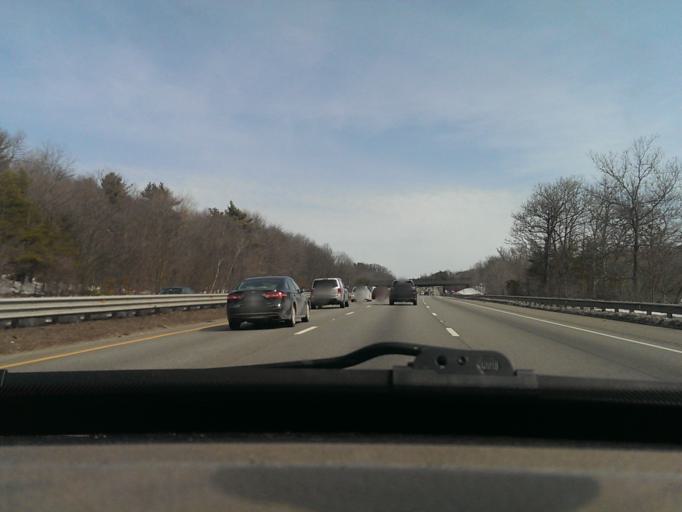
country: US
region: Massachusetts
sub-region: Worcester County
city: Charlton
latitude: 42.1529
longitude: -71.9832
